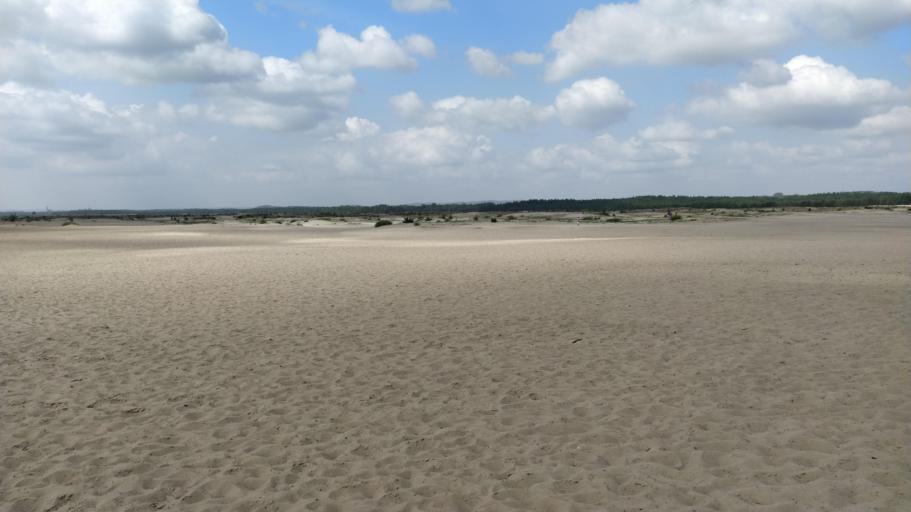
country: PL
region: Lesser Poland Voivodeship
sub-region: Powiat olkuski
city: Klucze
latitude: 50.3361
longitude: 19.5330
